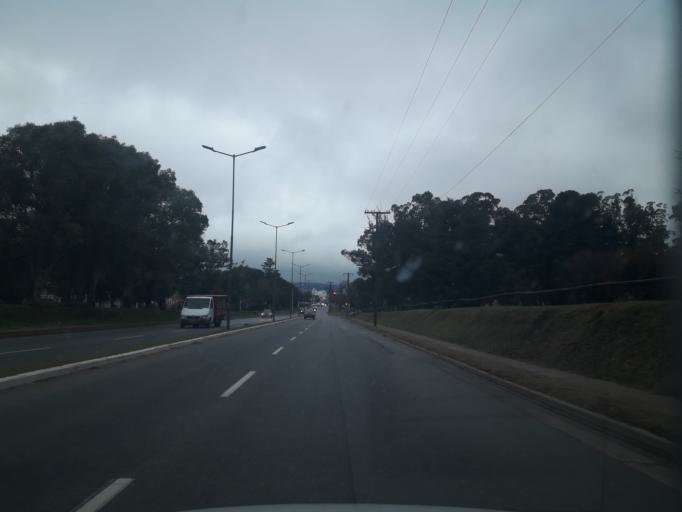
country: AR
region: Buenos Aires
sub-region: Partido de Tandil
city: Tandil
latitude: -37.3075
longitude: -59.1613
